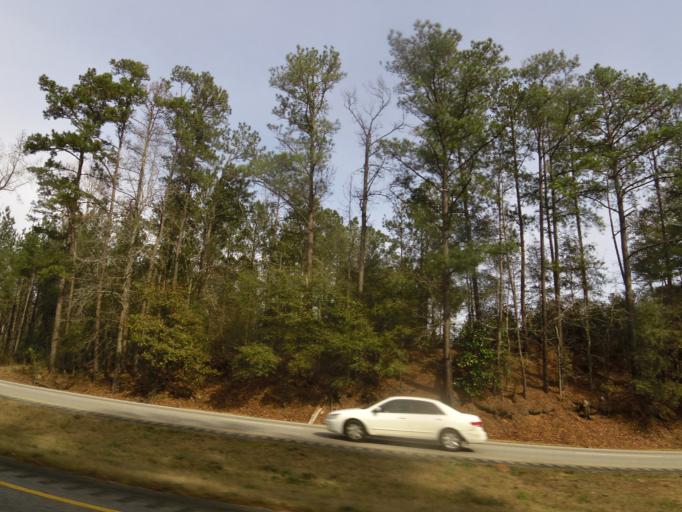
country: US
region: Alabama
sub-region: Dale County
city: Ozark
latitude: 31.4141
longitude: -85.6051
